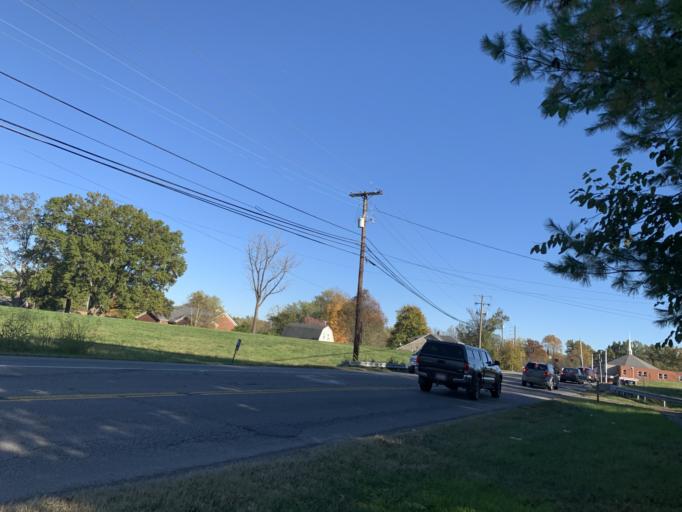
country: US
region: Kentucky
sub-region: Jefferson County
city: Pleasure Ridge Park
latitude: 38.1584
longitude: -85.8492
